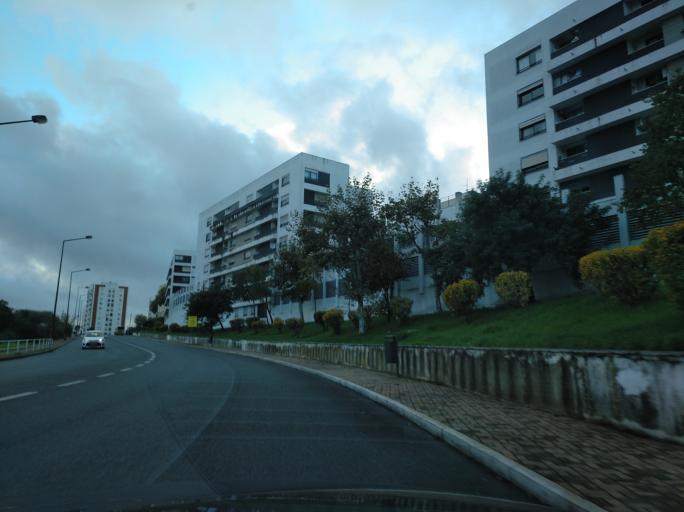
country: PT
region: Lisbon
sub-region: Loures
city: Moscavide
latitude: 38.7462
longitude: -9.1104
